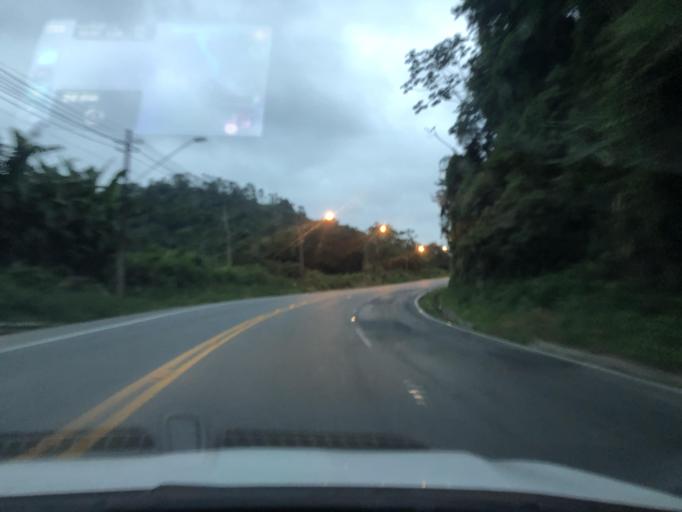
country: BR
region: Santa Catarina
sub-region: Pomerode
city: Pomerode
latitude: -26.7474
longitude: -49.0696
